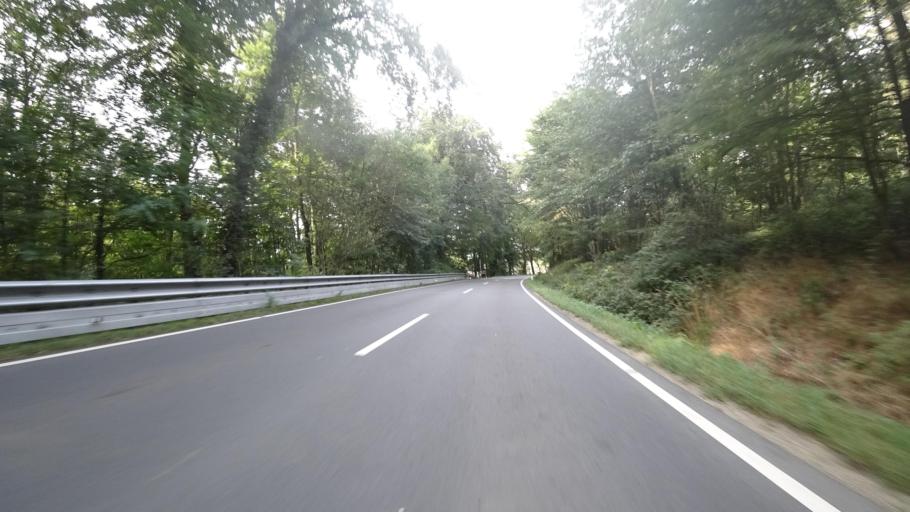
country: DE
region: North Rhine-Westphalia
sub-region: Regierungsbezirk Detmold
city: Steinhagen
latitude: 52.0179
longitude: 8.4512
